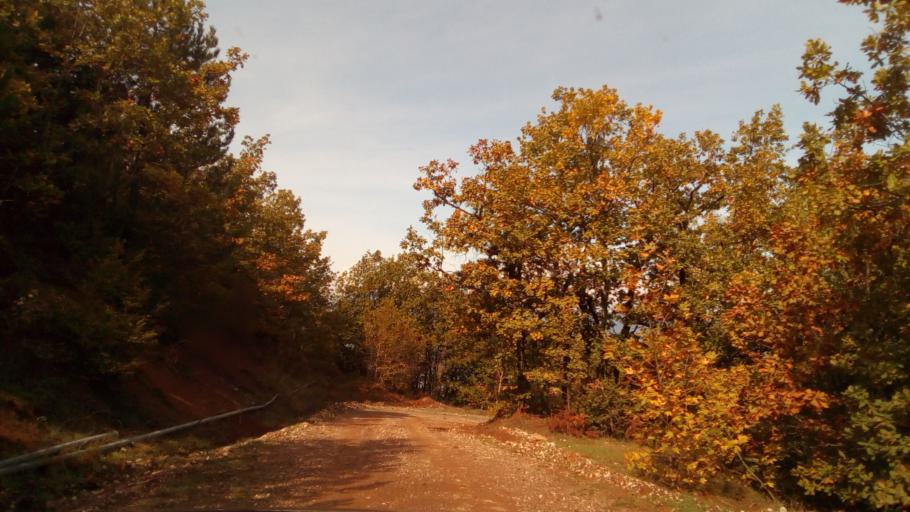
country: GR
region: West Greece
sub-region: Nomos Achaias
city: Kamarai
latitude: 38.4759
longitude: 22.0217
